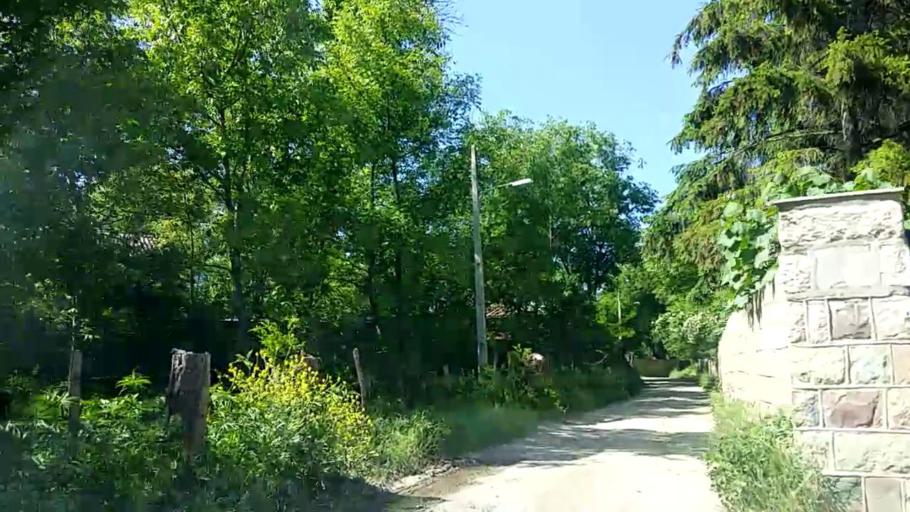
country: IR
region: Mazandaran
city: `Abbasabad
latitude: 36.5095
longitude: 51.1894
